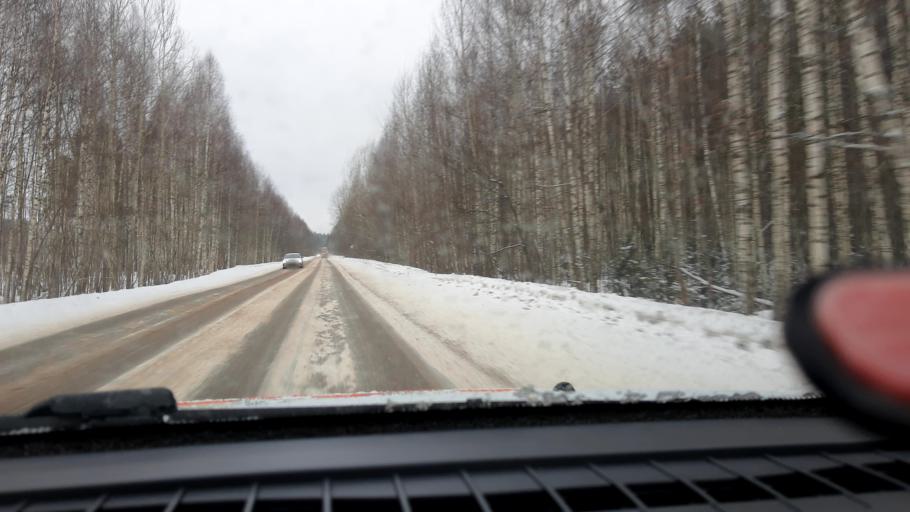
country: RU
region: Nizjnij Novgorod
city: Pamyat' Parizhskoy Kommuny
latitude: 56.2746
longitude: 44.4019
